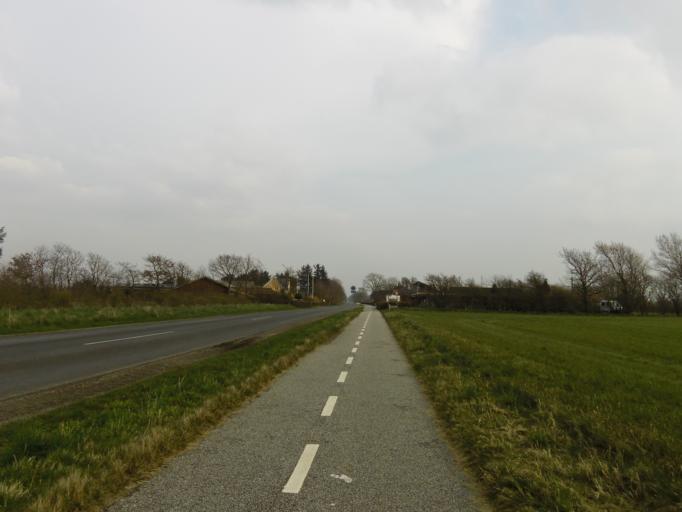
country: DK
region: South Denmark
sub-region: Esbjerg Kommune
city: Ribe
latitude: 55.3477
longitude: 8.7491
